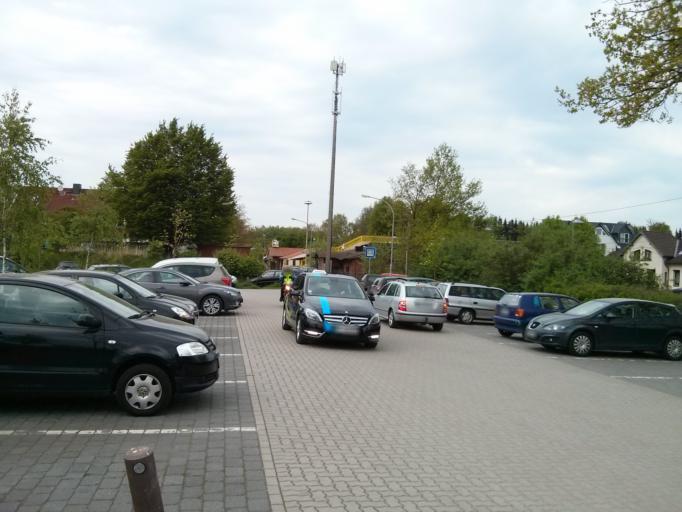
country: DE
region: Lower Saxony
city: Bendestorf
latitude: 53.3654
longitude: 9.9281
